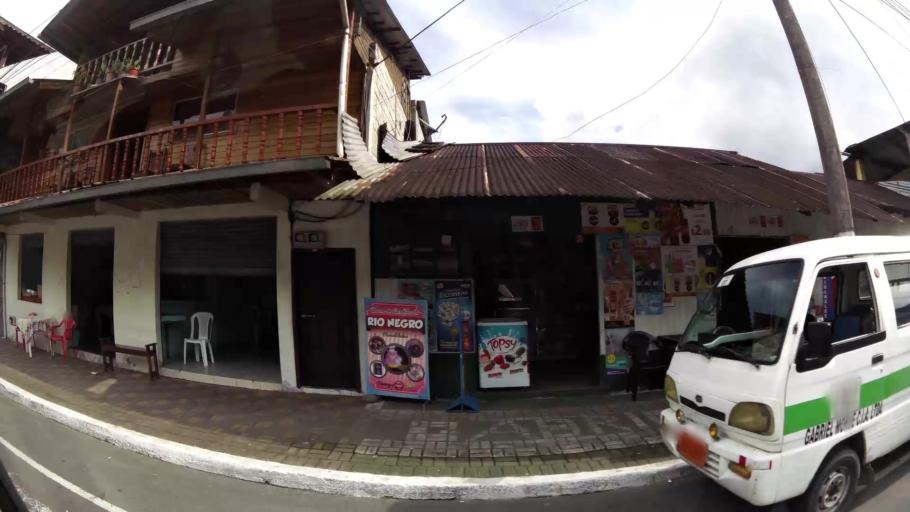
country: EC
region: Tungurahua
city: Banos
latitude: -1.4141
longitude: -78.2119
